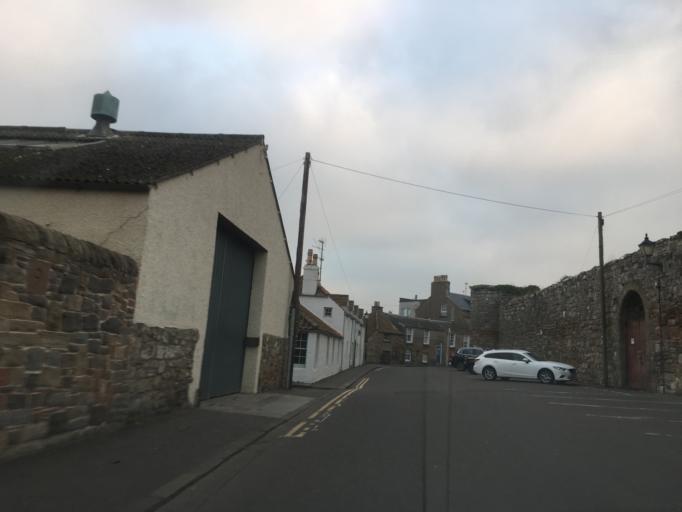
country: GB
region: Scotland
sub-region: Fife
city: Saint Andrews
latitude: 56.3374
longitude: -2.7841
